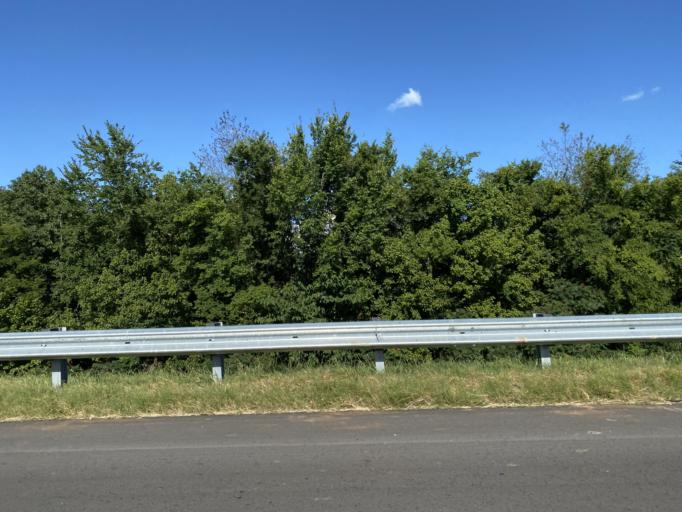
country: US
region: Alabama
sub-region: Limestone County
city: Athens
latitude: 34.7555
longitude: -86.9381
